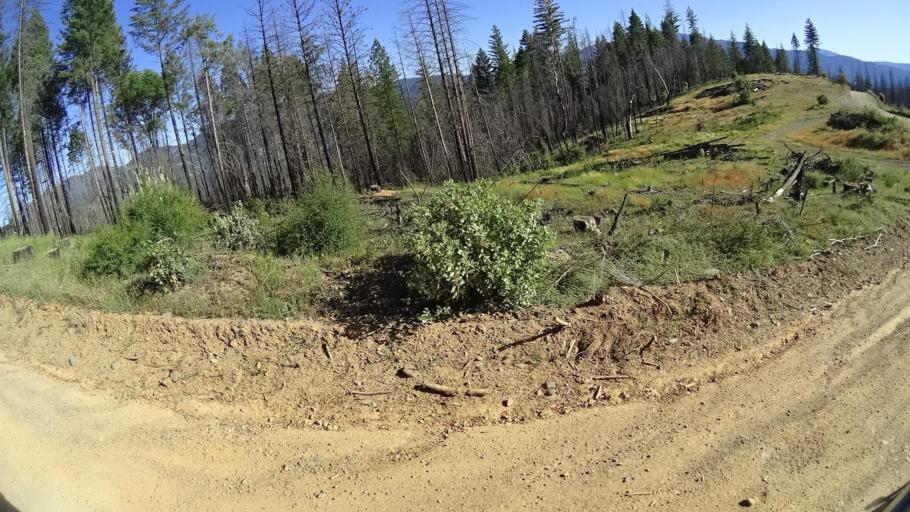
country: US
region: California
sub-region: Lake County
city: Upper Lake
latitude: 39.3864
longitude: -122.9816
